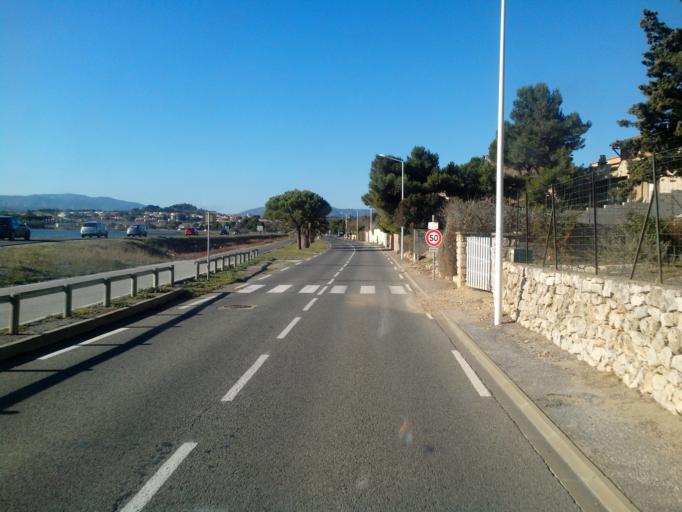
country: FR
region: Languedoc-Roussillon
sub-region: Departement de l'Aude
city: Leucate
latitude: 42.9042
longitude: 3.0465
